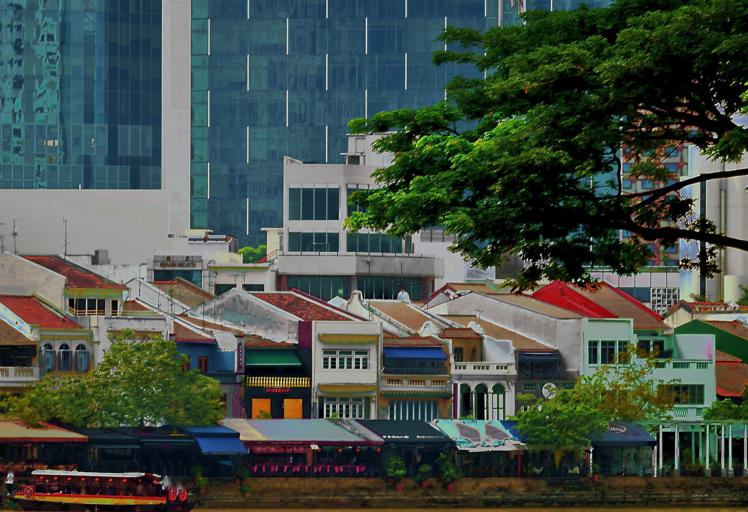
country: SG
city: Singapore
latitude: 1.2861
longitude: 103.8523
